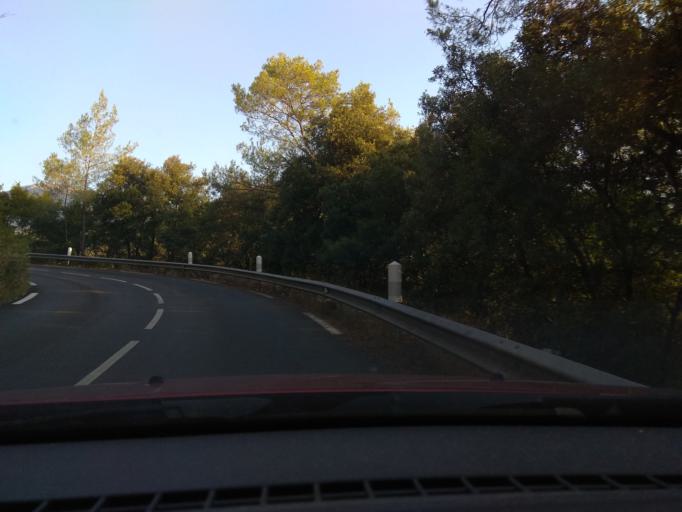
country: FR
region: Provence-Alpes-Cote d'Azur
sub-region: Departement des Alpes-Maritimes
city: La Colle-sur-Loup
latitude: 43.6877
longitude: 7.0701
